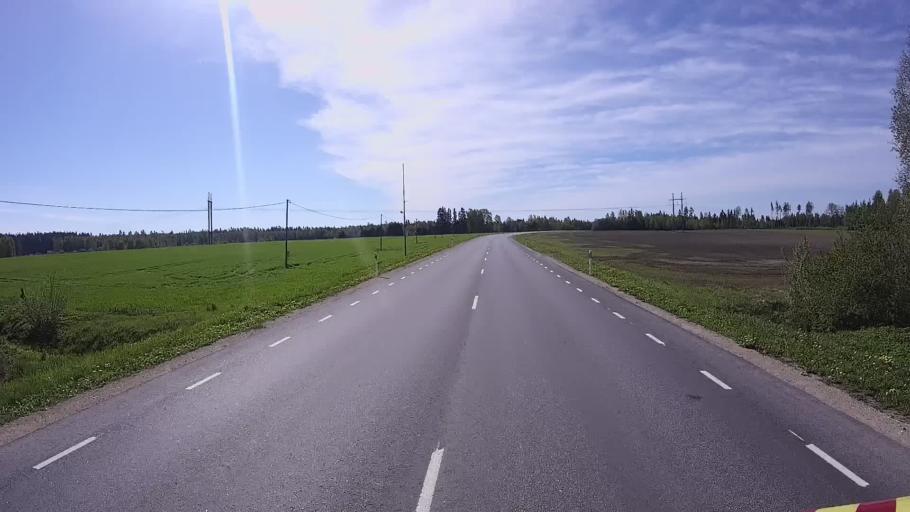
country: EE
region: Polvamaa
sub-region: Polva linn
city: Polva
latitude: 58.3111
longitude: 26.9946
